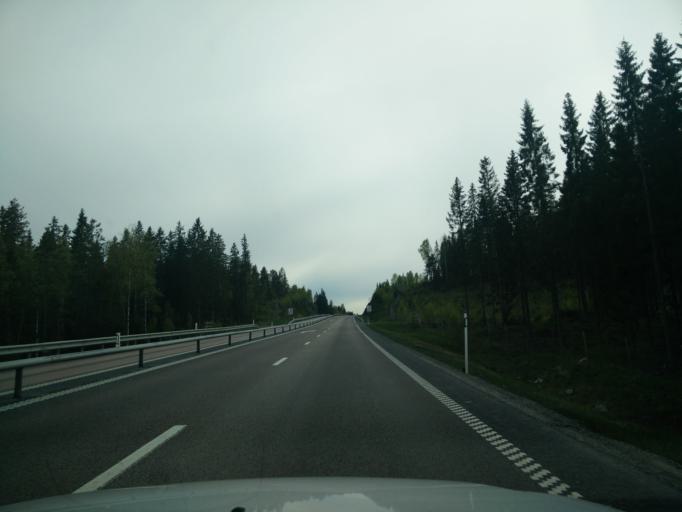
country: SE
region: Vaesternorrland
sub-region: OErnskoeldsviks Kommun
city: Bjasta
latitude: 63.1891
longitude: 18.4635
